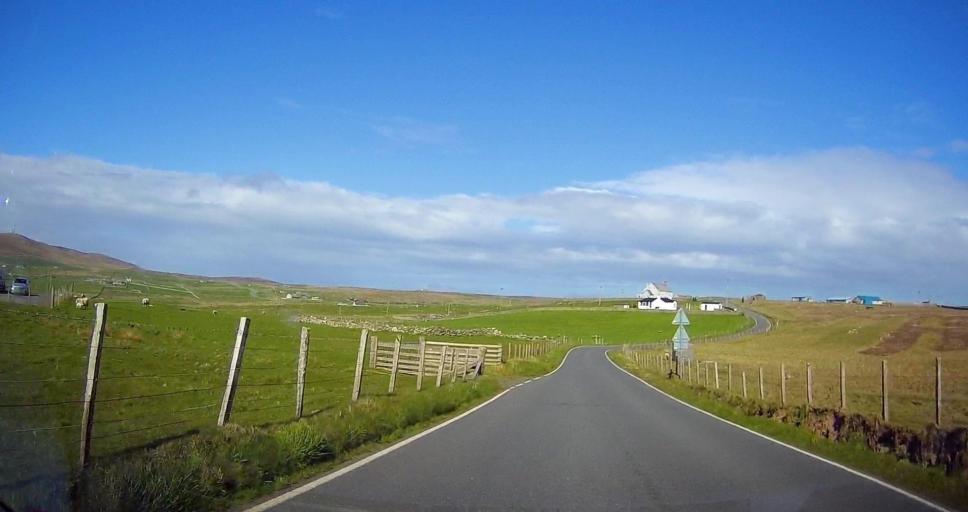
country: GB
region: Scotland
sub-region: Shetland Islands
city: Sandwick
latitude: 59.9183
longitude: -1.3083
